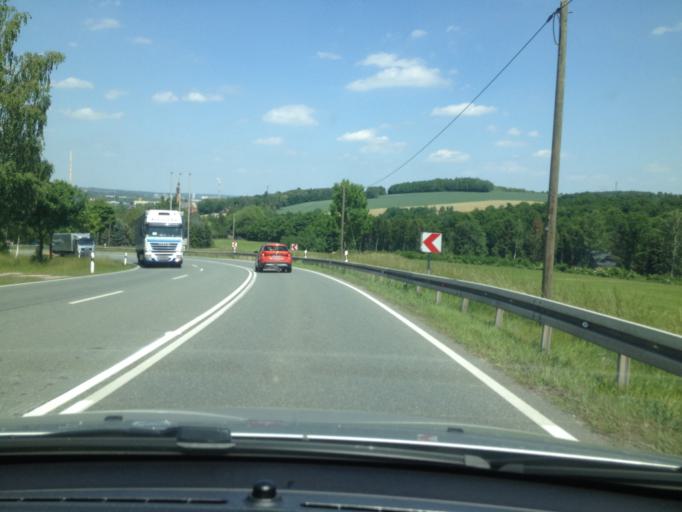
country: DE
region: Saxony
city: Burkhardtsdorf
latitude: 50.7707
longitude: 12.9281
